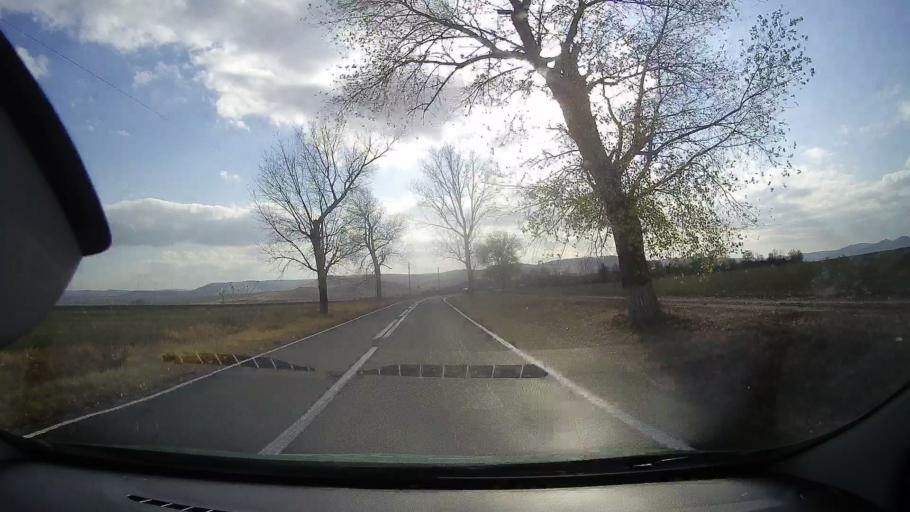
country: RO
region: Tulcea
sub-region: Comuna Nalbant
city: Nicolae Balcescu
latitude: 45.0044
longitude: 28.5972
